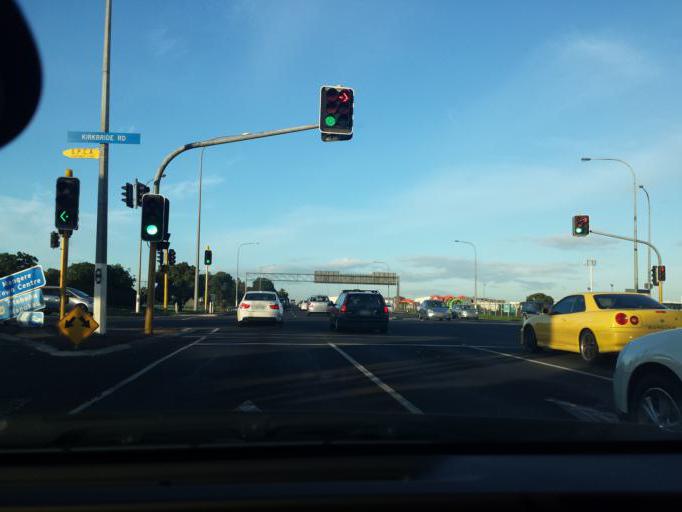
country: NZ
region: Auckland
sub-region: Auckland
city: Mangere
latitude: -36.9735
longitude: 174.7896
